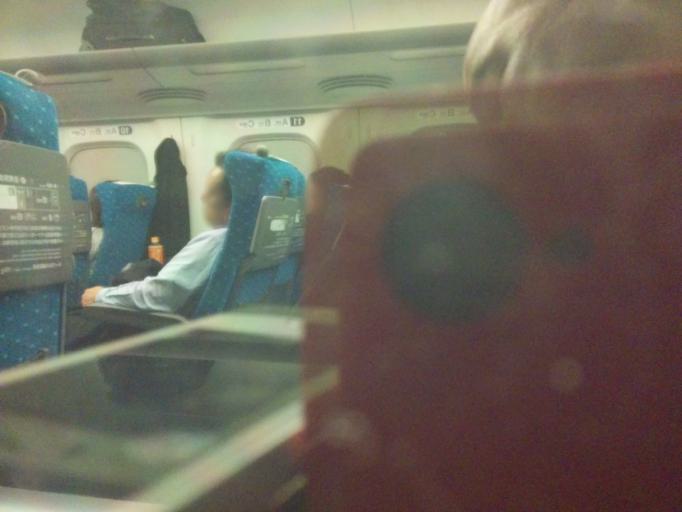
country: JP
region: Shizuoka
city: Fujinomiya
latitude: 35.1044
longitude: 138.5510
